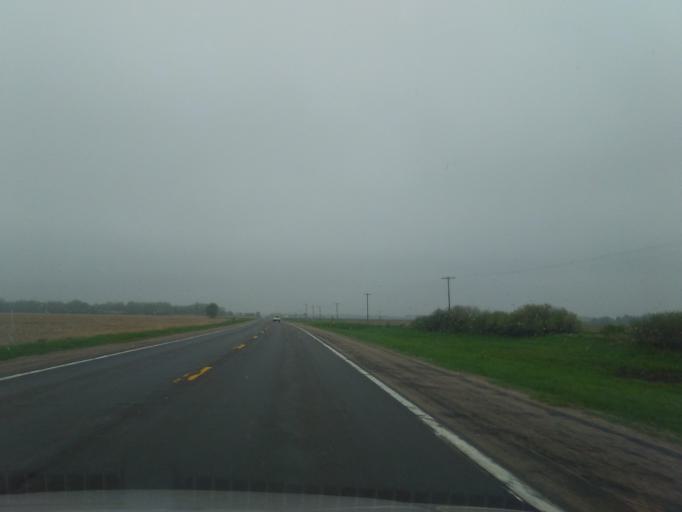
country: US
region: Nebraska
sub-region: Cuming County
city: West Point
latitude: 41.9010
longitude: -96.7629
